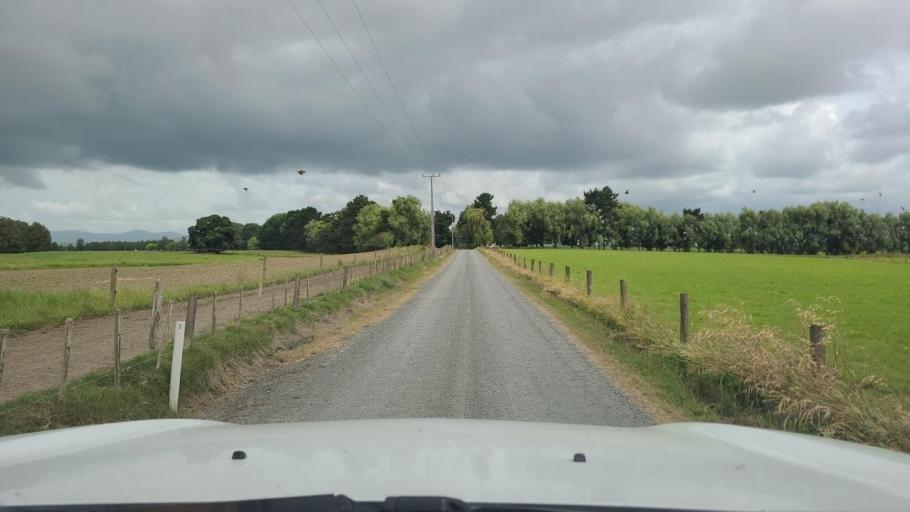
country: NZ
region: Waikato
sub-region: Hauraki District
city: Paeroa
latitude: -37.5057
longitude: 175.5850
